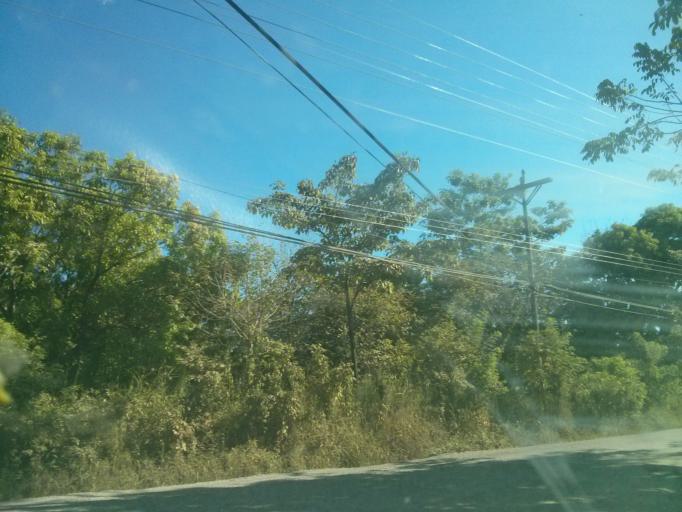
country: CR
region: Puntarenas
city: Paquera
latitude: 9.6794
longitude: -85.1188
